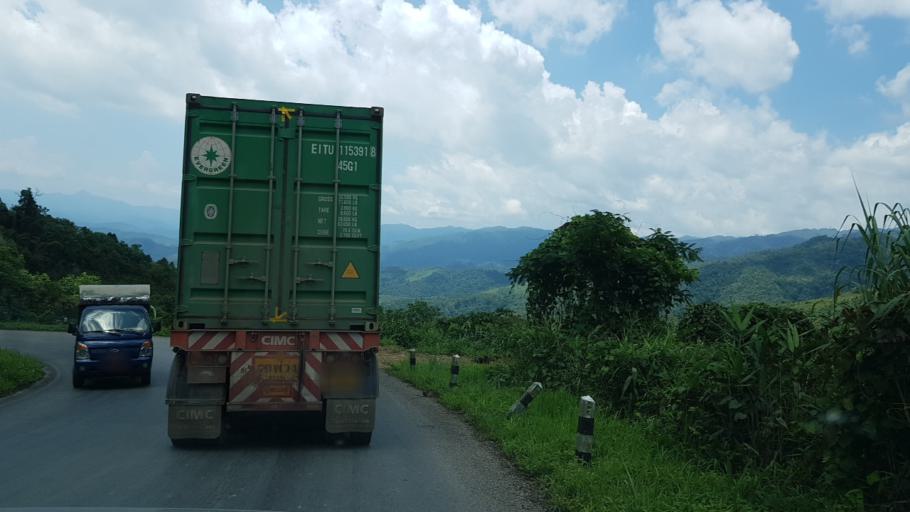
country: LA
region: Vientiane
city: Muang Kasi
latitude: 19.3716
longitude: 102.1601
